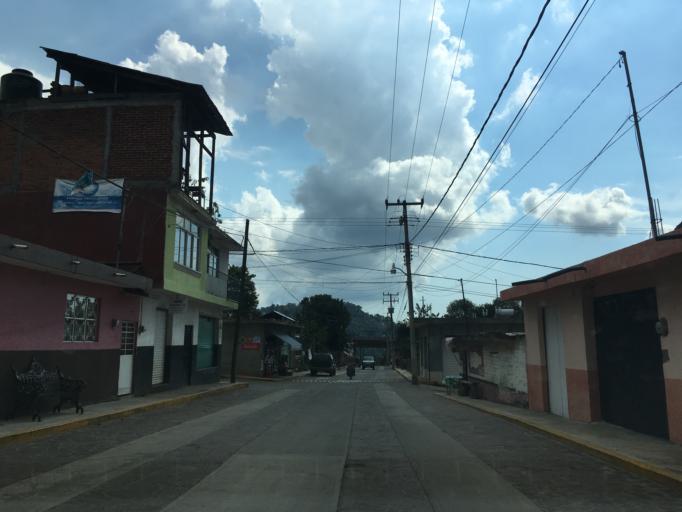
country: MX
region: Michoacan
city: Tingambato
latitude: 19.4991
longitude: -101.8552
